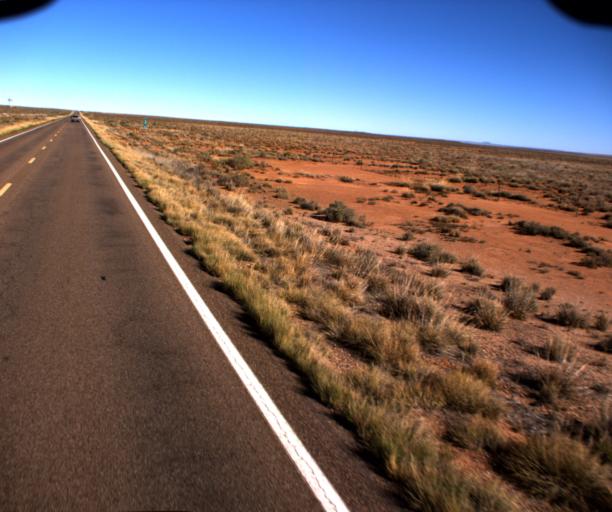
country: US
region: Arizona
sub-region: Navajo County
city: Holbrook
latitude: 34.7253
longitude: -110.1153
